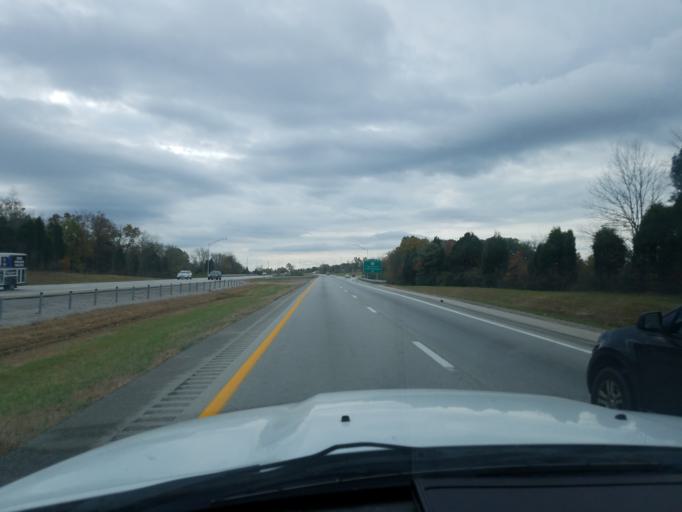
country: US
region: Kentucky
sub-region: Jefferson County
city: Jeffersontown
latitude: 38.1943
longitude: -85.5087
